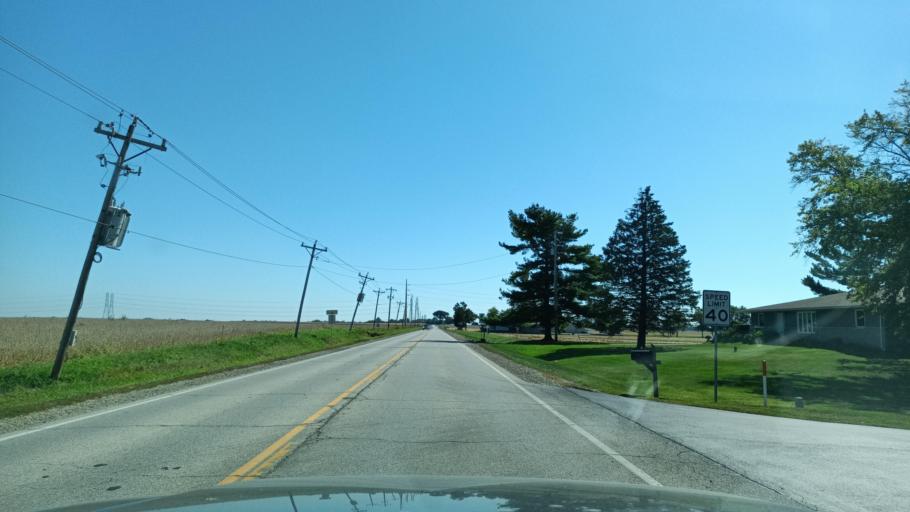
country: US
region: Illinois
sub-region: Peoria County
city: Dunlap
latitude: 40.7896
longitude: -89.7458
